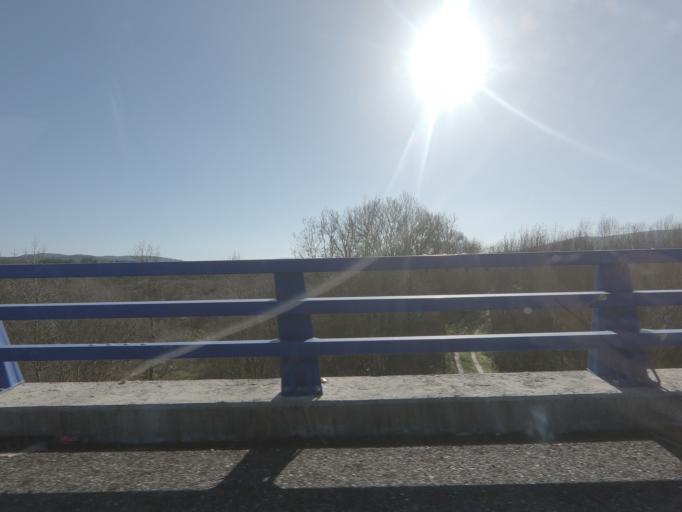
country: ES
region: Galicia
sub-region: Provincia de Ourense
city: Verin
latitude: 41.9112
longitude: -7.4395
